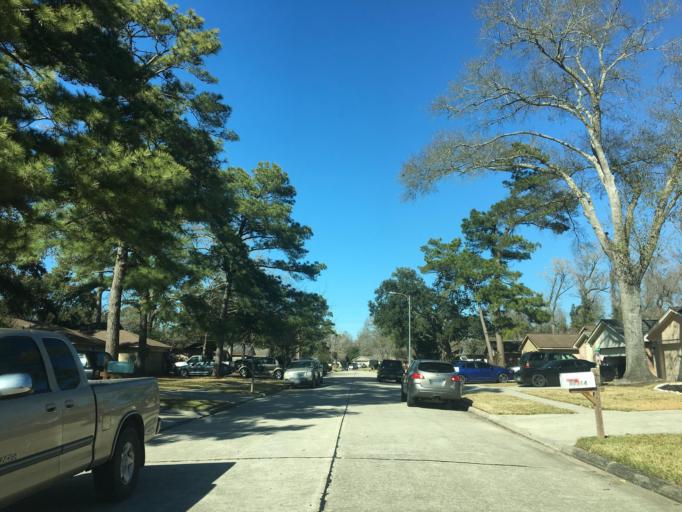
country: US
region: Texas
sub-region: Harris County
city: Spring
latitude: 30.0872
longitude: -95.4660
